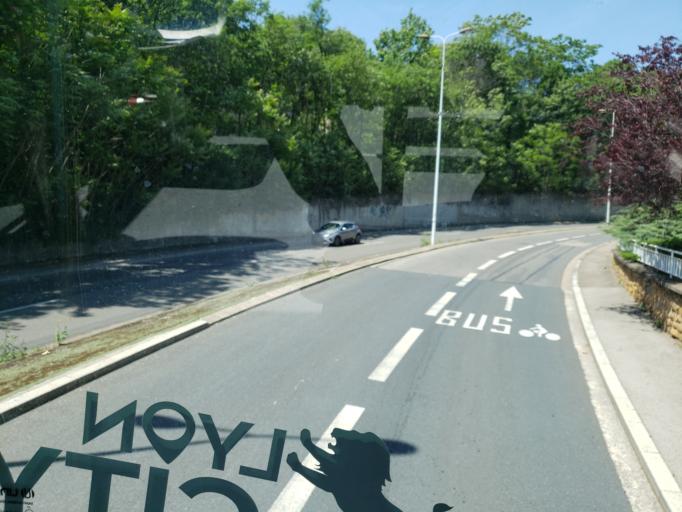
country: FR
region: Rhone-Alpes
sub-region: Departement du Rhone
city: Sainte-Foy-les-Lyon
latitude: 45.7512
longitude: 4.8139
